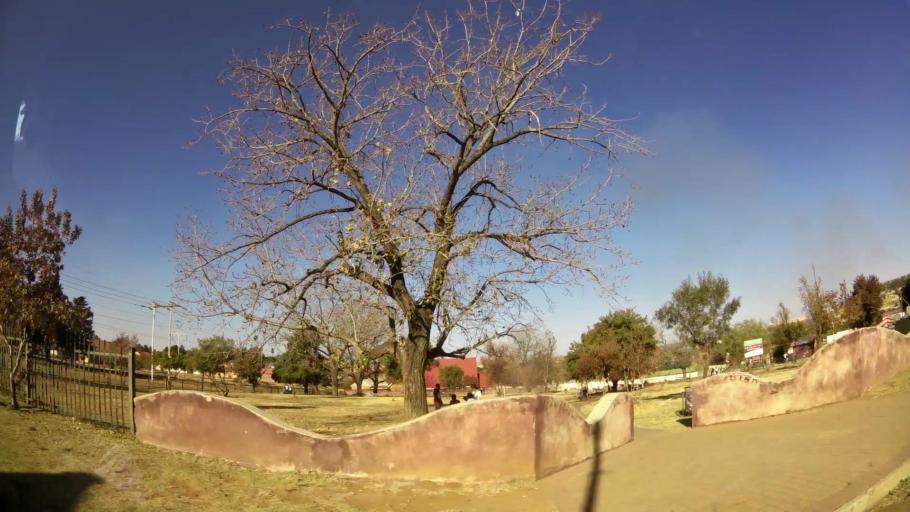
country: ZA
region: Gauteng
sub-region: City of Johannesburg Metropolitan Municipality
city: Johannesburg
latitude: -26.2113
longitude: 27.9735
